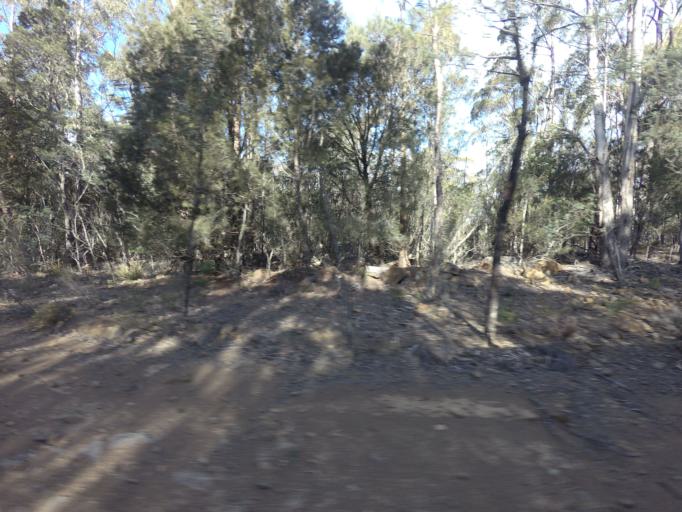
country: AU
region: Tasmania
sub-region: Break O'Day
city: St Helens
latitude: -41.8393
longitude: 148.0605
